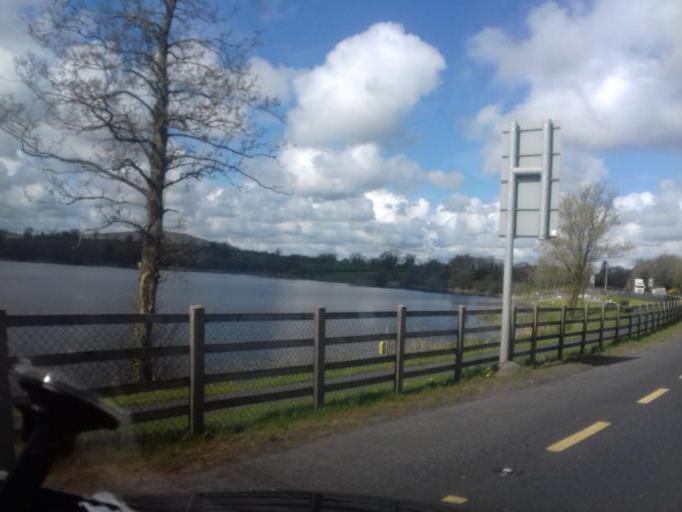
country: IE
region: Ulster
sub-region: An Cabhan
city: Ballyjamesduff
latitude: 53.9695
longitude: -7.2341
